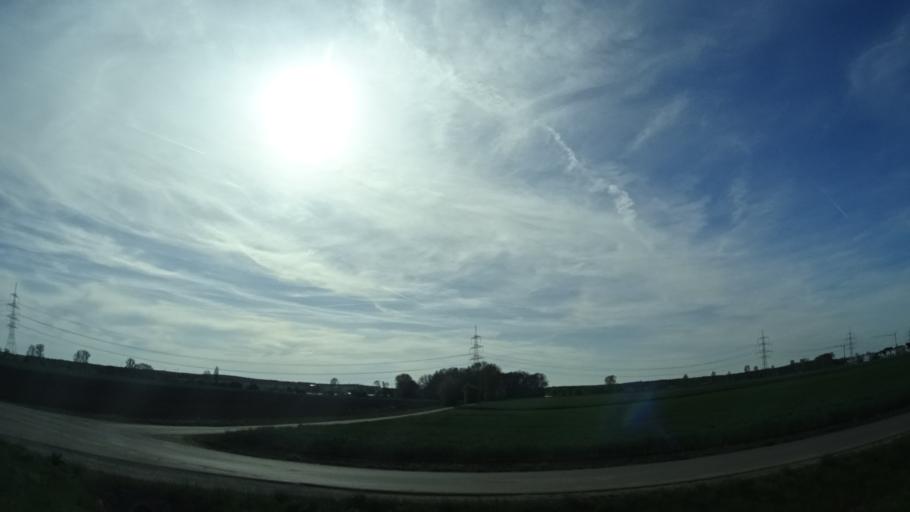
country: DE
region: Bavaria
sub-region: Regierungsbezirk Unterfranken
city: Kolitzheim
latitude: 49.9453
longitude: 10.2617
